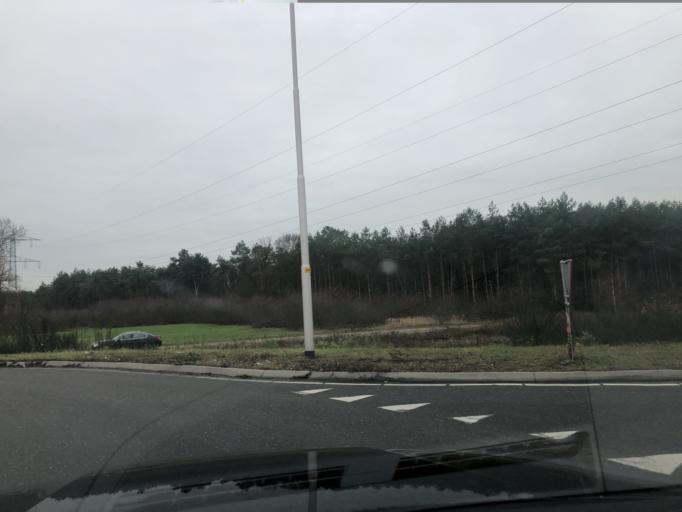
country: NL
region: North Brabant
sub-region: Gemeente Oss
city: Berghem
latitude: 51.7313
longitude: 5.5693
